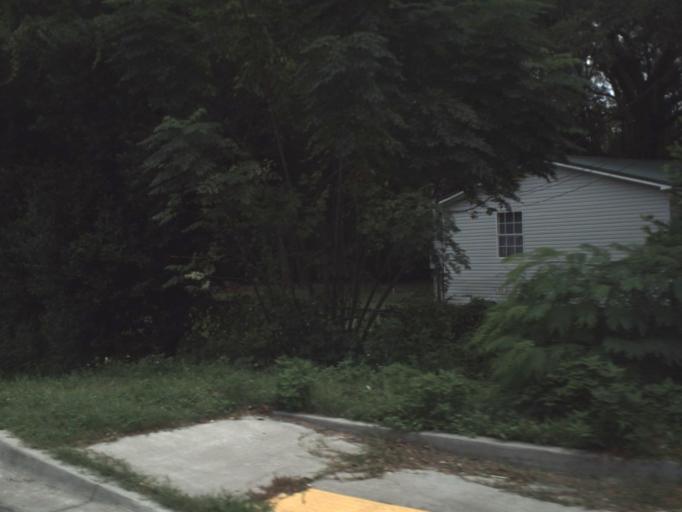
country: US
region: Florida
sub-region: Bay County
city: Hiland Park
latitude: 30.2332
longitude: -85.5948
